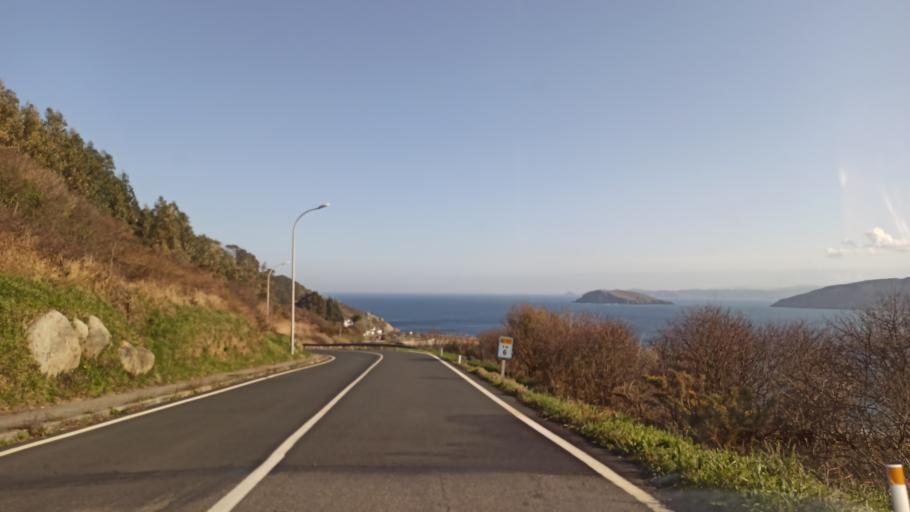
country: ES
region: Galicia
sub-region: Provincia da Coruna
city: Manon
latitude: 43.7722
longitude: -7.6794
